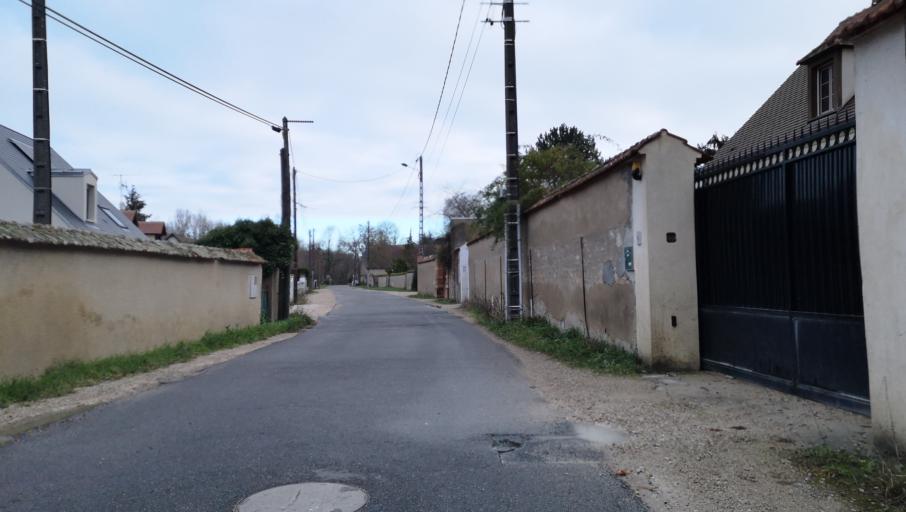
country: FR
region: Centre
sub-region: Departement du Loiret
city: Saint-Jean-de-Braye
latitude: 47.9059
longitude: 1.9939
